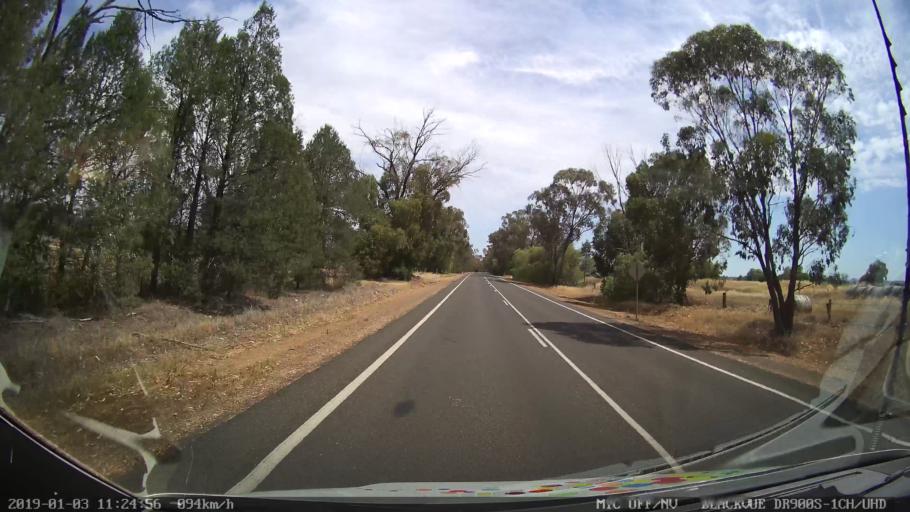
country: AU
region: New South Wales
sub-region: Weddin
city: Grenfell
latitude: -34.0452
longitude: 148.2319
